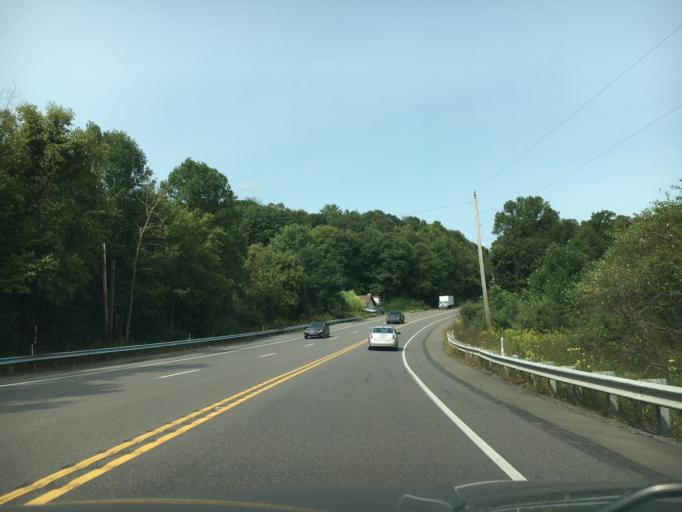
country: US
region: Pennsylvania
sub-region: Carbon County
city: Summit Hill
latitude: 40.7081
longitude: -75.8263
